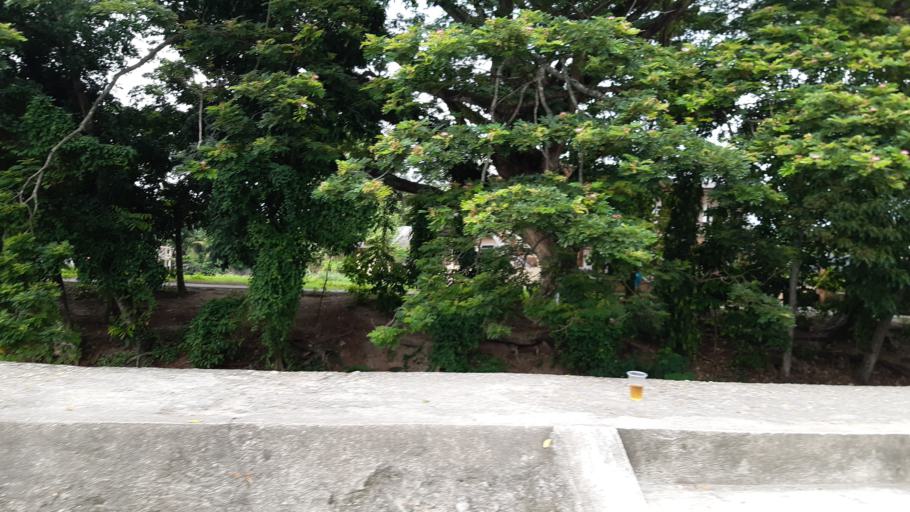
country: PH
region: Central Visayas
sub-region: Province of Negros Oriental
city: Dumaguete
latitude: 9.3047
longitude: 123.2986
